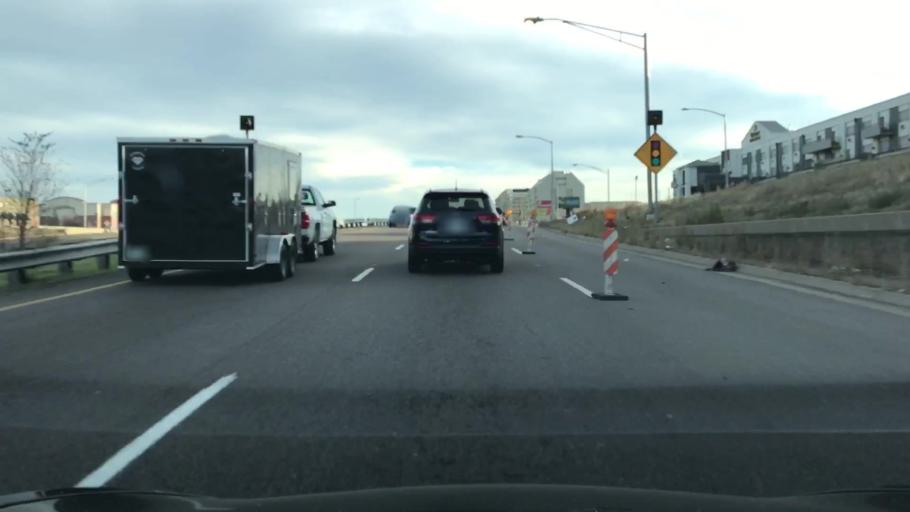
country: US
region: Colorado
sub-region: Adams County
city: Commerce City
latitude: 39.7698
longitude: -104.9033
